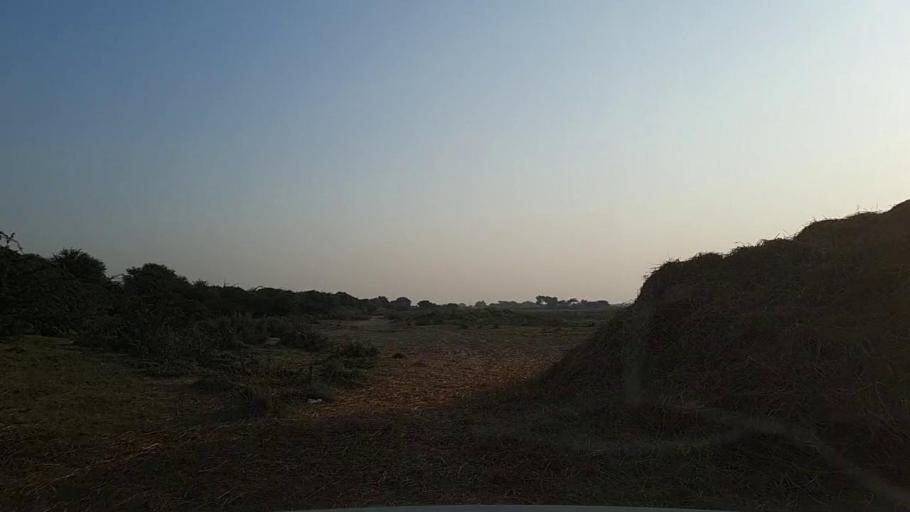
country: PK
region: Sindh
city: Daro Mehar
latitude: 24.7349
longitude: 68.1813
